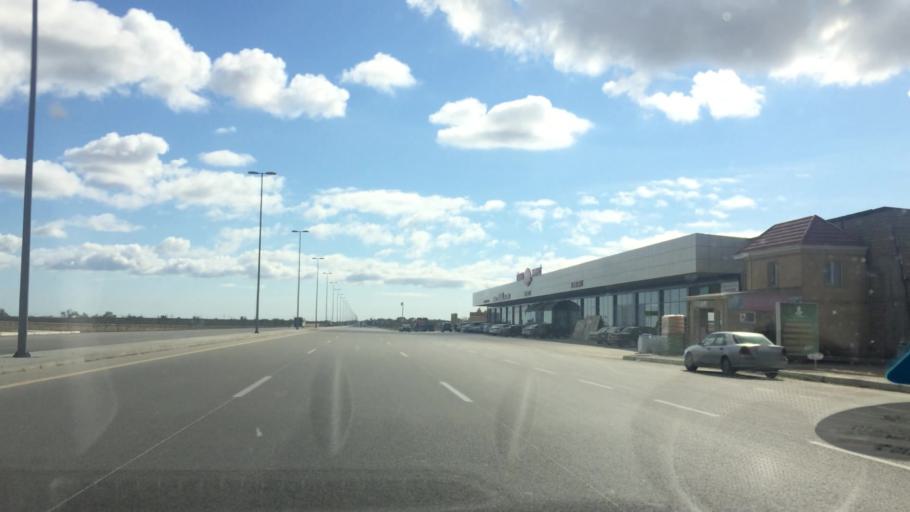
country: AZ
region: Baki
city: Qala
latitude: 40.4568
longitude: 50.1422
